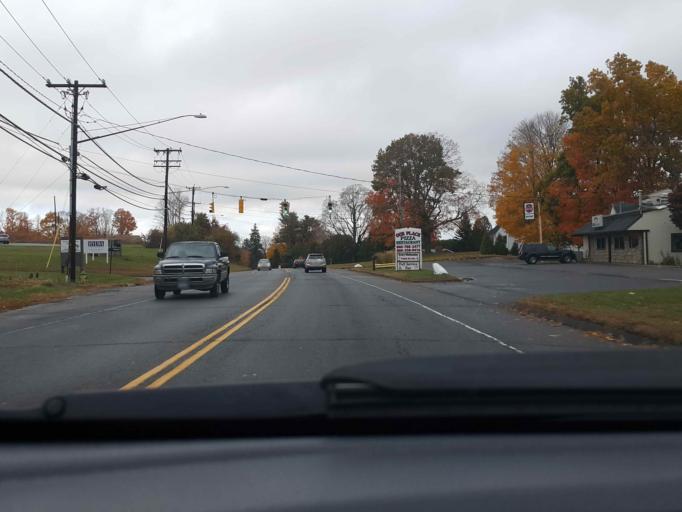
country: US
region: Connecticut
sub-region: Middlesex County
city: Durham
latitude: 41.5029
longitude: -72.6730
